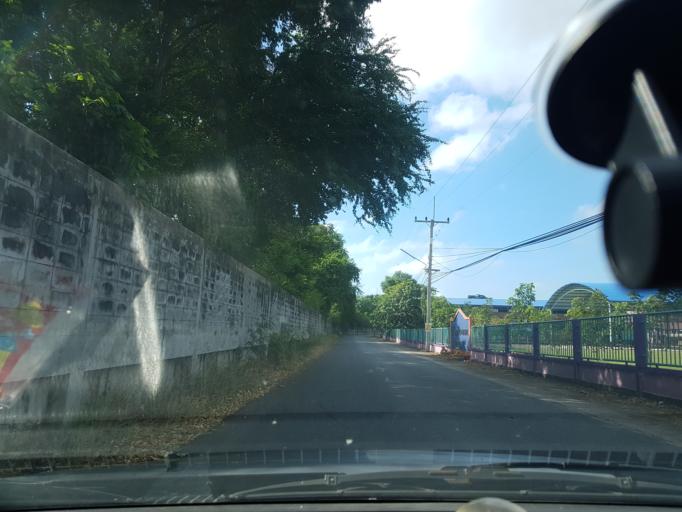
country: TH
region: Lop Buri
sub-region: Amphoe Tha Luang
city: Tha Luang
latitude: 15.0760
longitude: 101.0518
